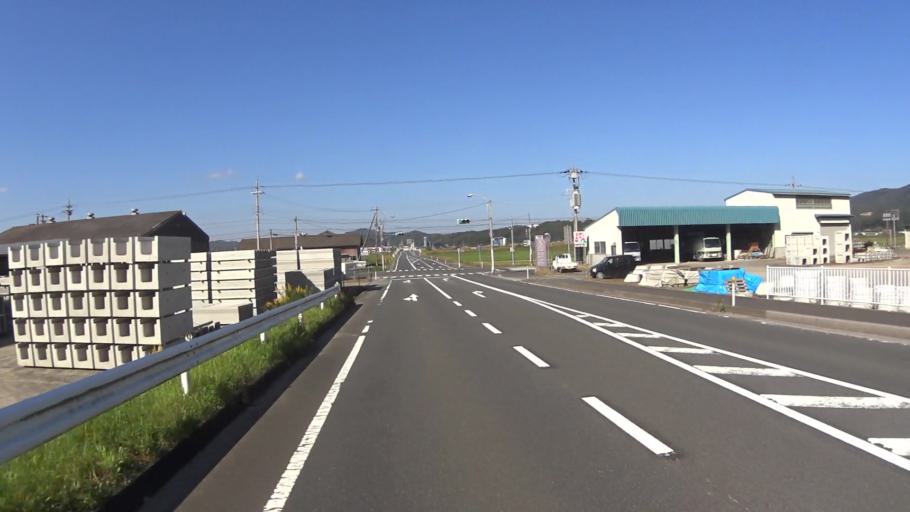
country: JP
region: Kyoto
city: Miyazu
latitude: 35.6694
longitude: 135.0928
